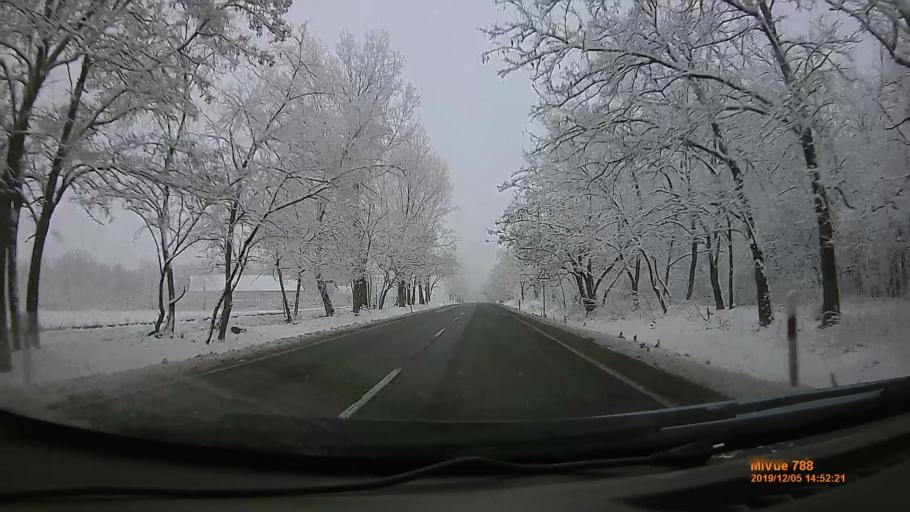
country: HU
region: Szabolcs-Szatmar-Bereg
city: Nyirtelek
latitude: 48.0005
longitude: 21.6457
